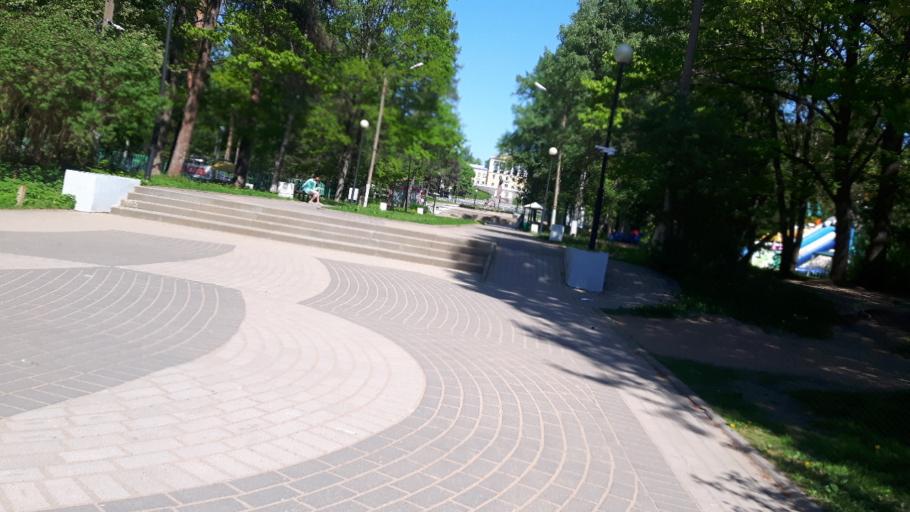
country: RU
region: St.-Petersburg
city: Zelenogorsk
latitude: 60.1910
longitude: 29.7009
